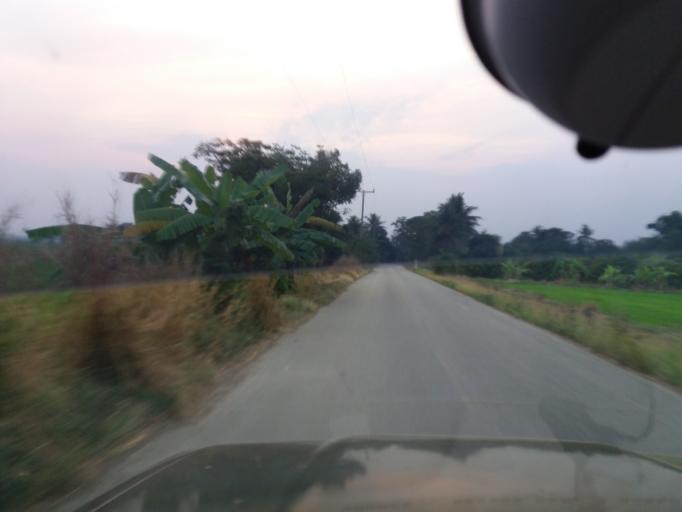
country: TH
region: Suphan Buri
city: Doem Bang Nang Buat
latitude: 14.8870
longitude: 100.1448
